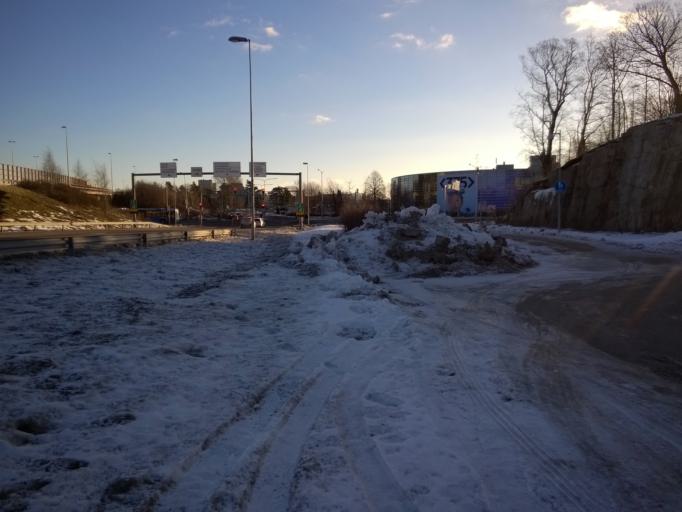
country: FI
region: Uusimaa
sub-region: Helsinki
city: Vantaa
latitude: 60.2281
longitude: 25.0098
